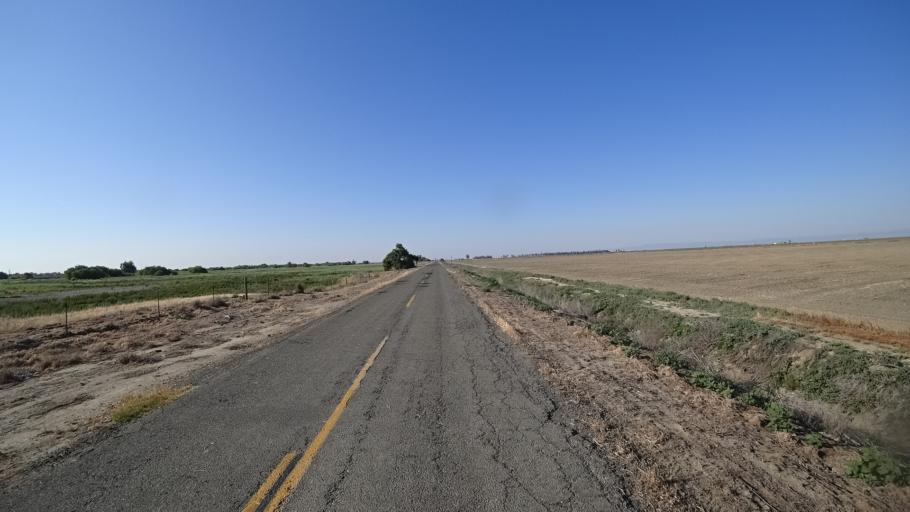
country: US
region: California
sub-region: Fresno County
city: Riverdale
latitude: 36.4004
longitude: -119.9278
